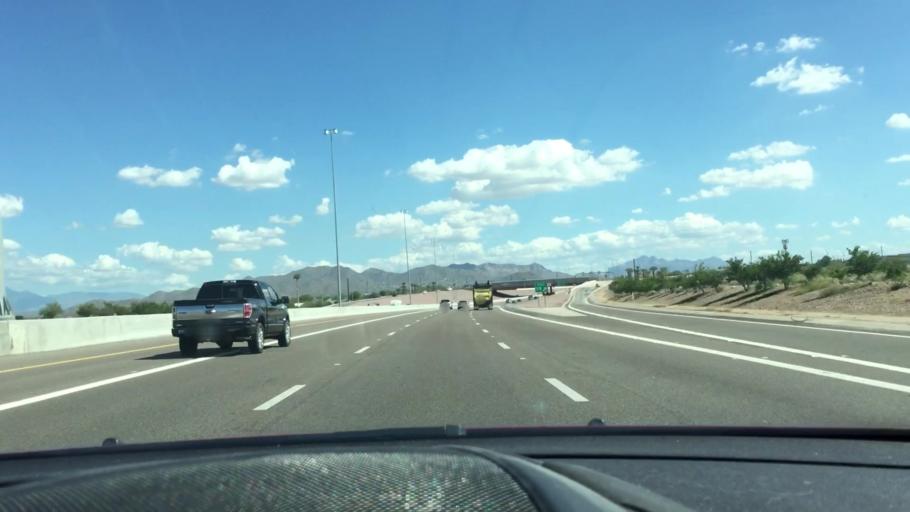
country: US
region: Arizona
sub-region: Maricopa County
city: Mesa
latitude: 33.4826
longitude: -111.7594
